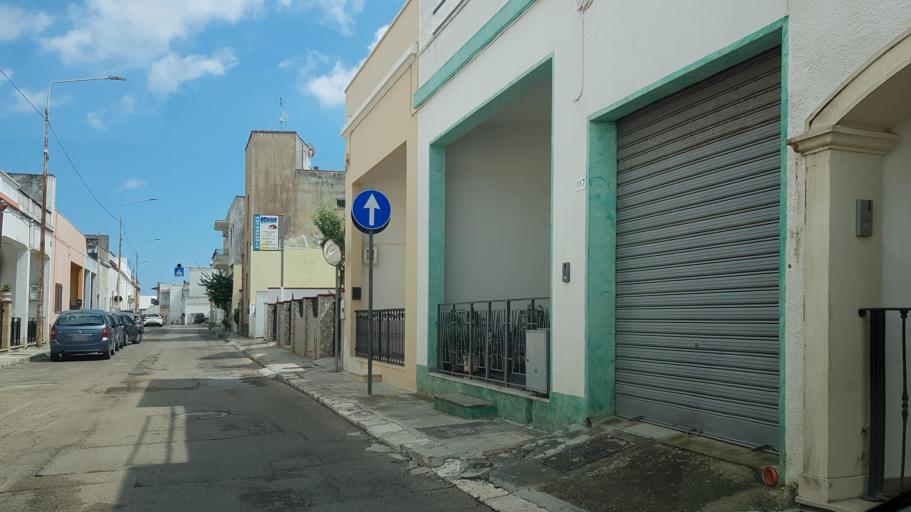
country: IT
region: Apulia
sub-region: Provincia di Lecce
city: Castrignano del Capo
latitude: 39.8364
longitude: 18.3476
